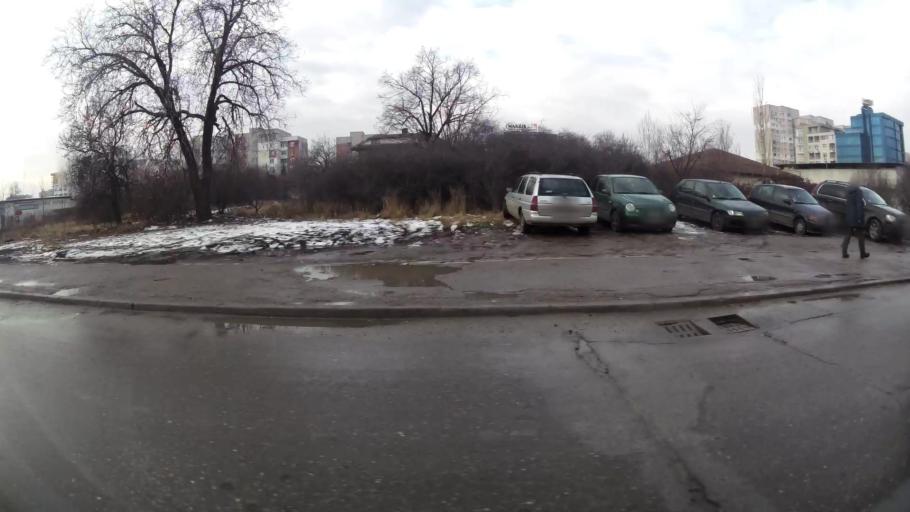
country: BG
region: Sofiya
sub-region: Obshtina Bozhurishte
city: Bozhurishte
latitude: 42.7302
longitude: 23.2557
